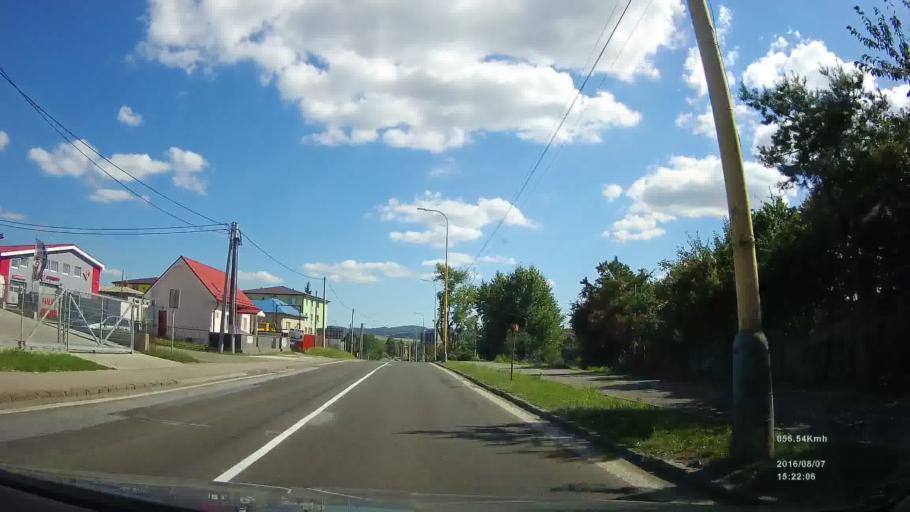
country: SK
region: Presovsky
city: Stropkov
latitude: 49.1953
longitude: 21.6542
